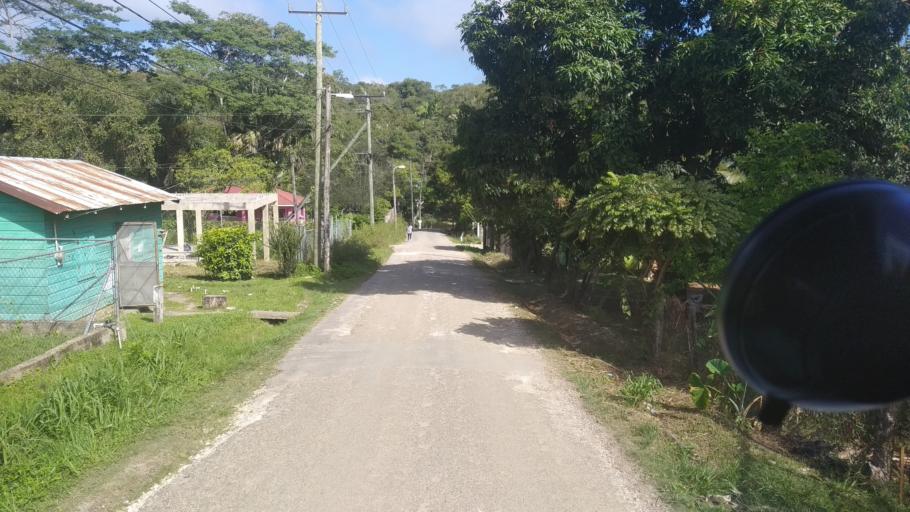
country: BZ
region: Cayo
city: Benque Viejo del Carmen
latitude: 17.0852
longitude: -89.1312
